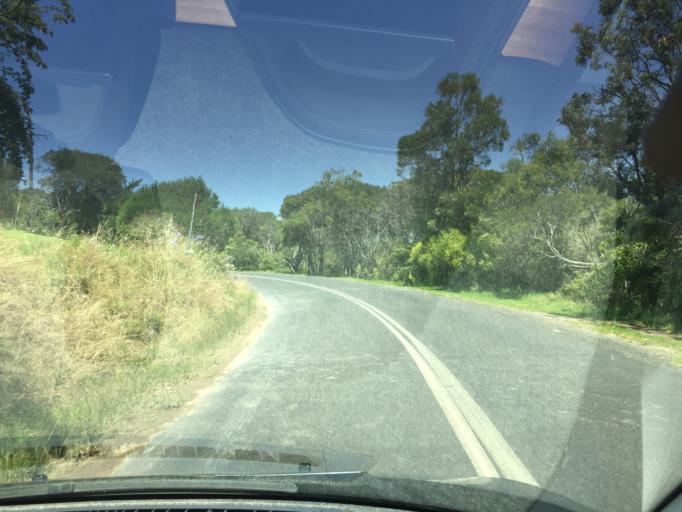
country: AU
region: New South Wales
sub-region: Bega Valley
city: Merimbula
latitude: -36.8942
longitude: 149.9245
